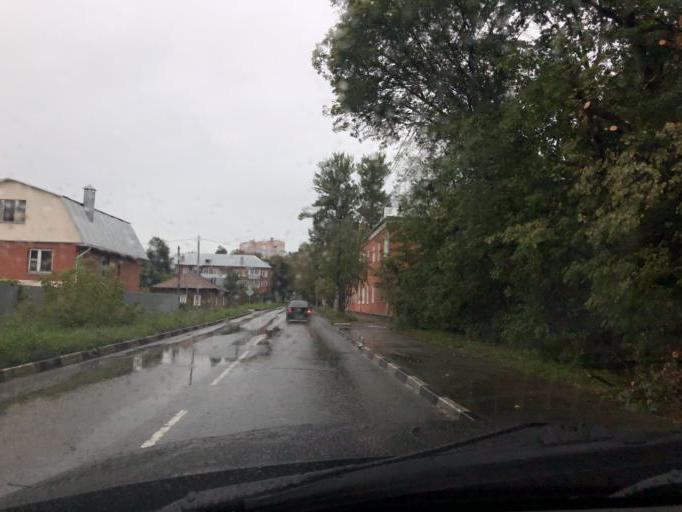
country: RU
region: Tula
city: Tula
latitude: 54.2257
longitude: 37.6235
